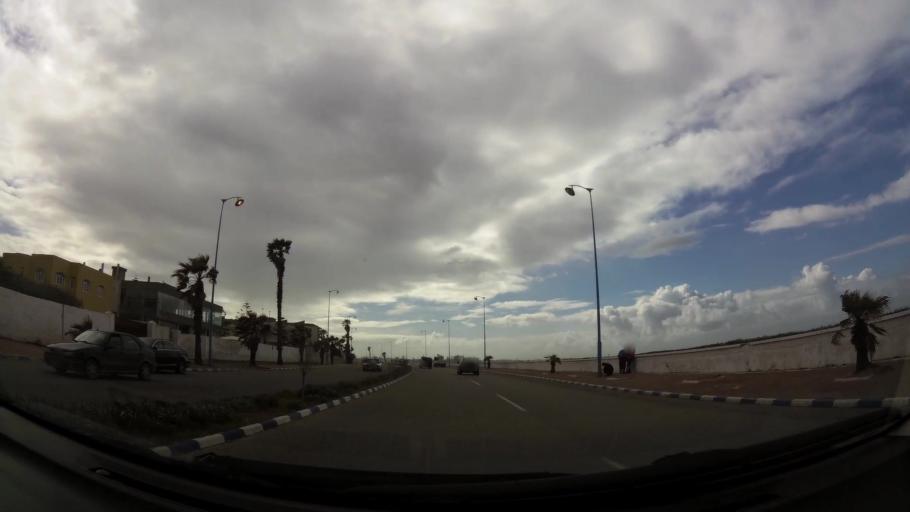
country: MA
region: Doukkala-Abda
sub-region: El-Jadida
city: El Jadida
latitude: 33.2445
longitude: -8.4783
